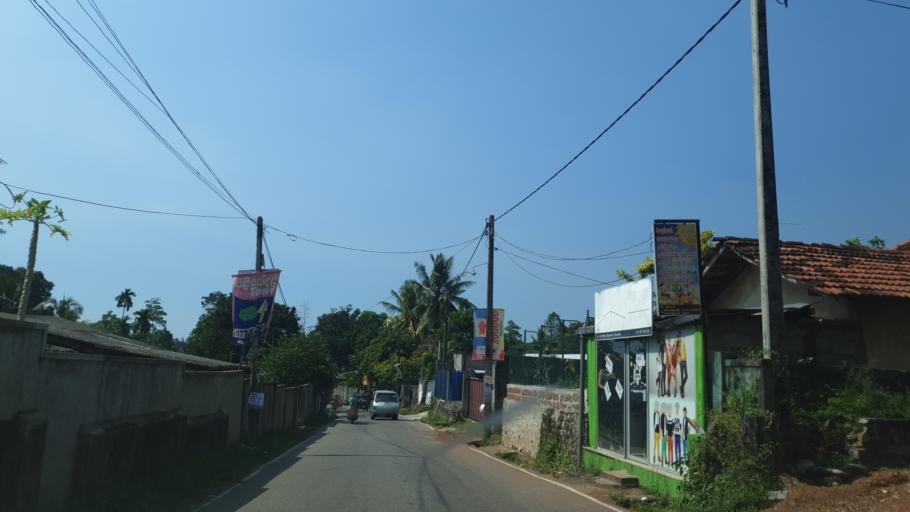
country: LK
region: Western
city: Moratuwa
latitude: 6.7652
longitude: 79.9349
